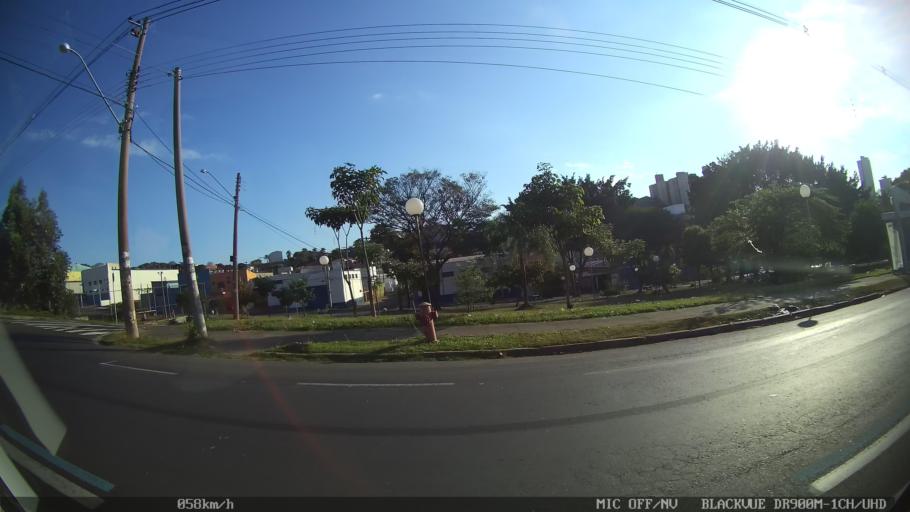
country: BR
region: Sao Paulo
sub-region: Piracicaba
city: Piracicaba
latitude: -22.7537
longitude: -47.6433
